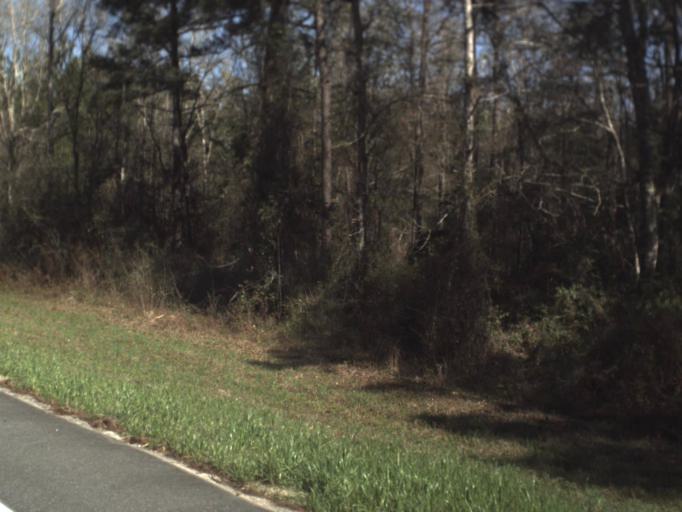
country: US
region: Florida
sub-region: Calhoun County
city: Blountstown
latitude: 30.2982
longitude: -85.1312
